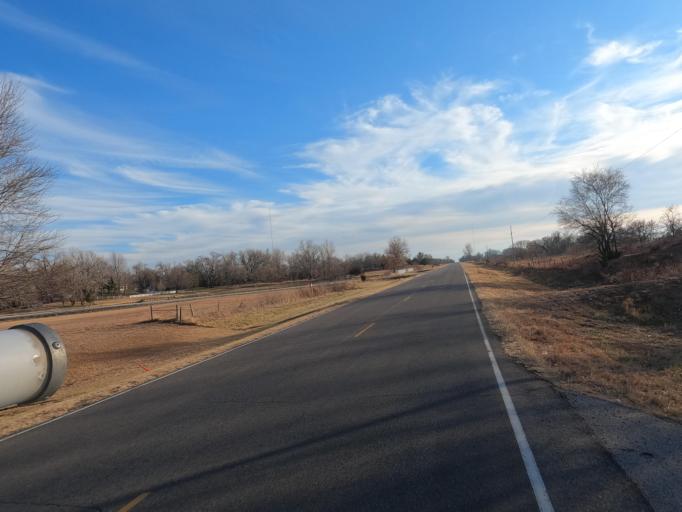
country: US
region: Kansas
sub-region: Reno County
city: Buhler
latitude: 38.0826
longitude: -97.7754
